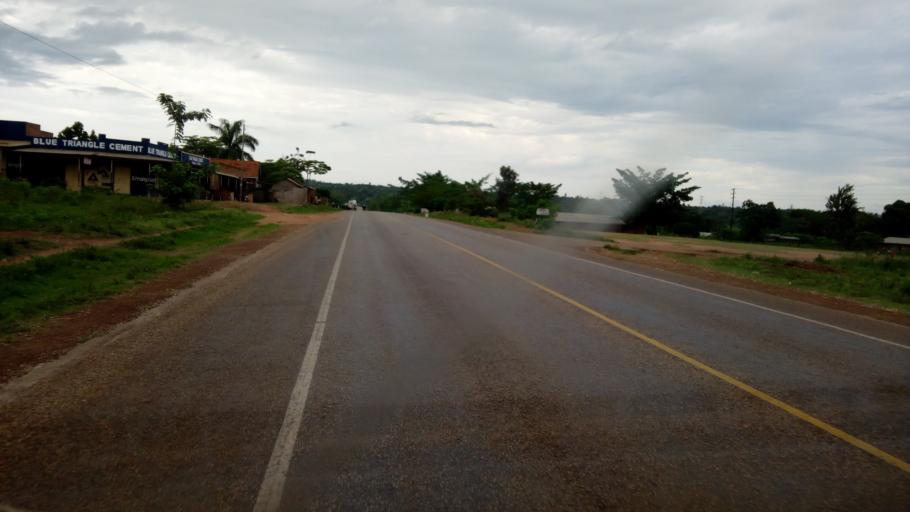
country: UG
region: Eastern Region
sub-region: Mbale District
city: Mbale
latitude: 0.9929
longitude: 34.1669
